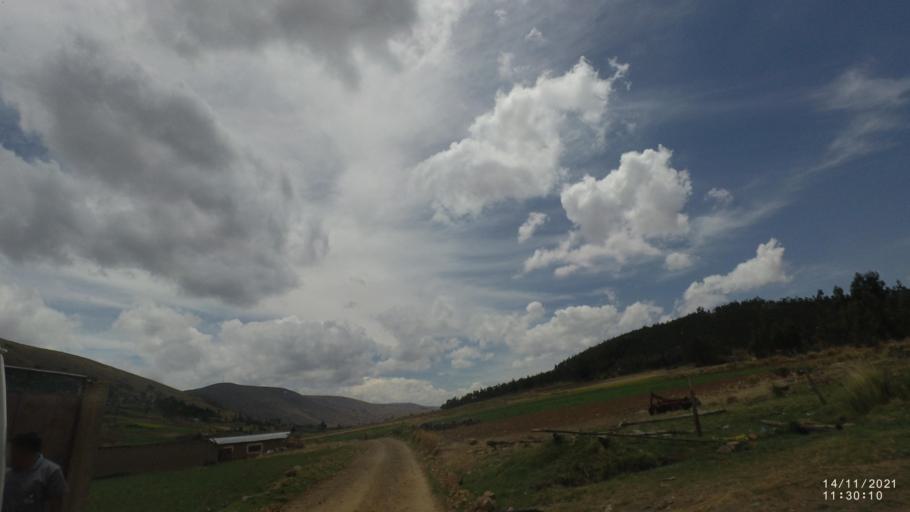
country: BO
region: Cochabamba
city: Colomi
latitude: -17.3440
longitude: -66.0113
